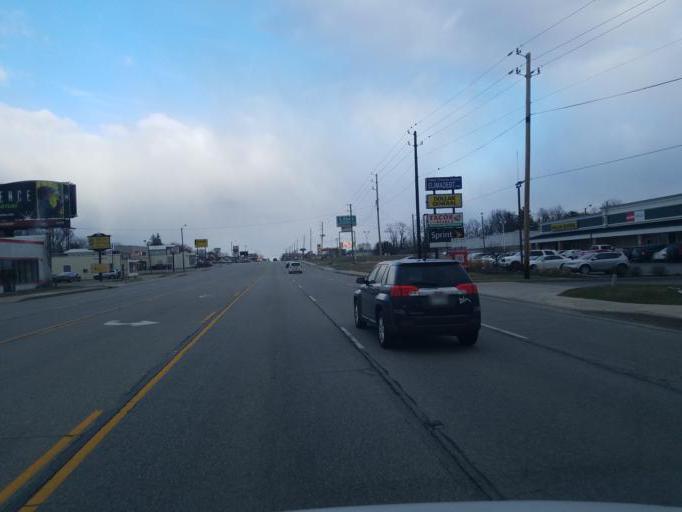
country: US
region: Indiana
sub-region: Marion County
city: Warren Park
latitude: 39.7733
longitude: -86.0211
